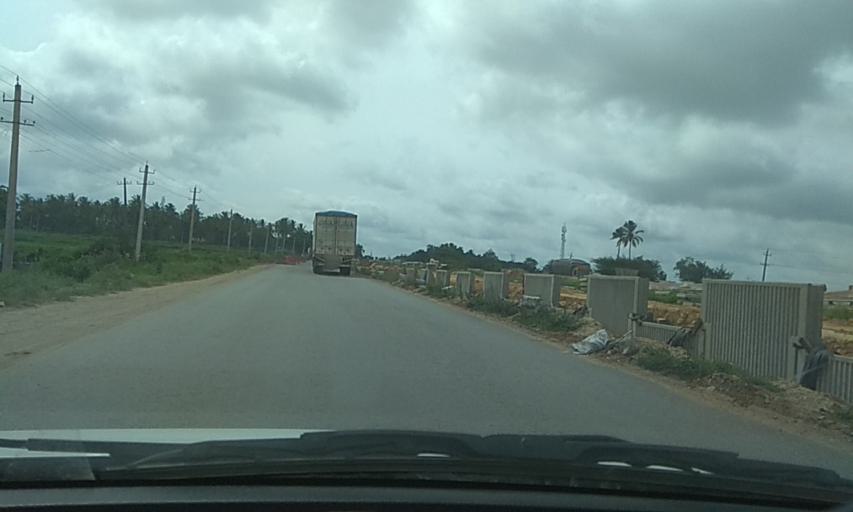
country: IN
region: Karnataka
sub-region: Davanagere
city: Mayakonda
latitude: 14.4252
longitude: 75.9745
